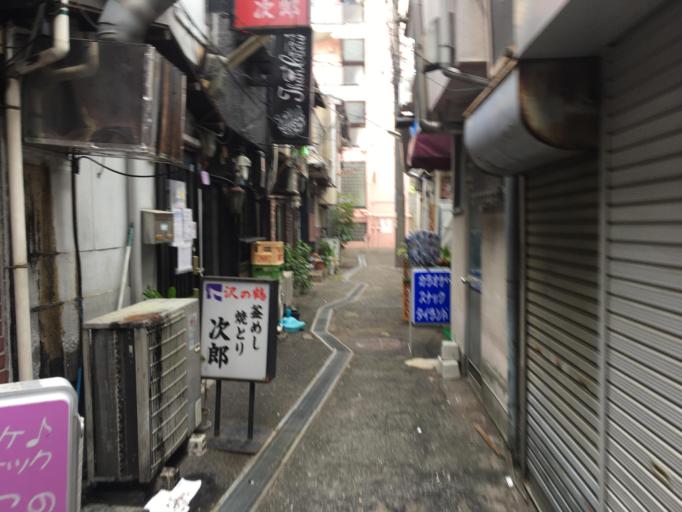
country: JP
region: Hyogo
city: Kobe
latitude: 34.6784
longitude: 135.1687
